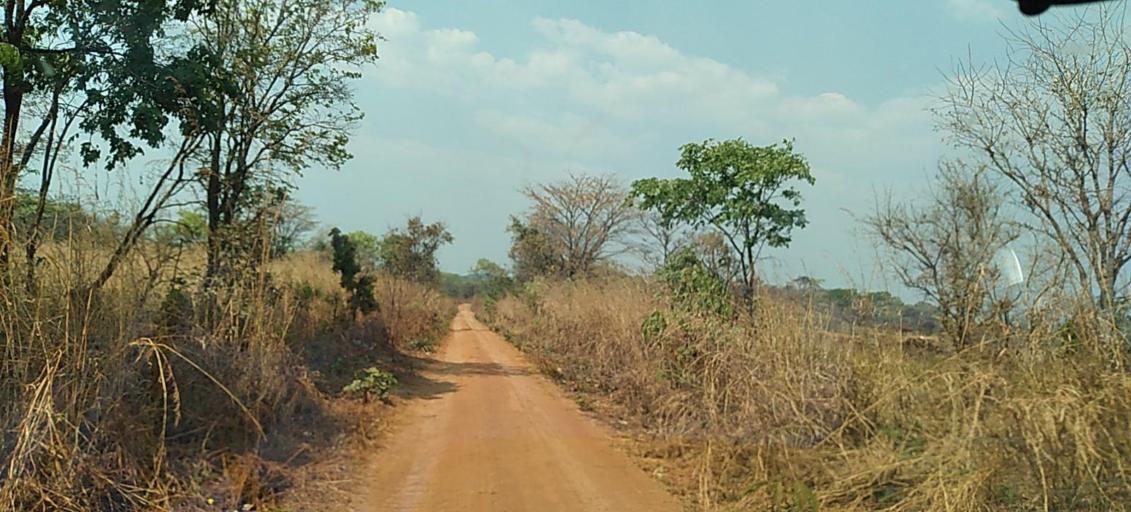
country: ZM
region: North-Western
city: Kasempa
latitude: -13.3085
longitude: 26.0671
